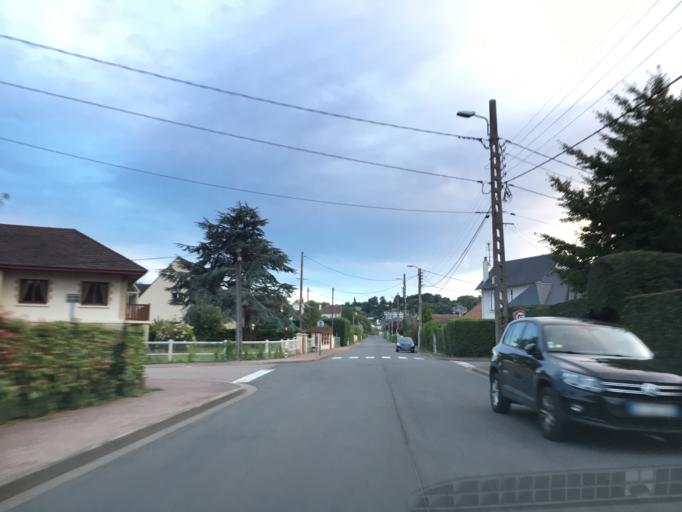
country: FR
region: Lower Normandy
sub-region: Departement du Calvados
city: Villers-sur-Mer
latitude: 49.3252
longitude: 0.0048
